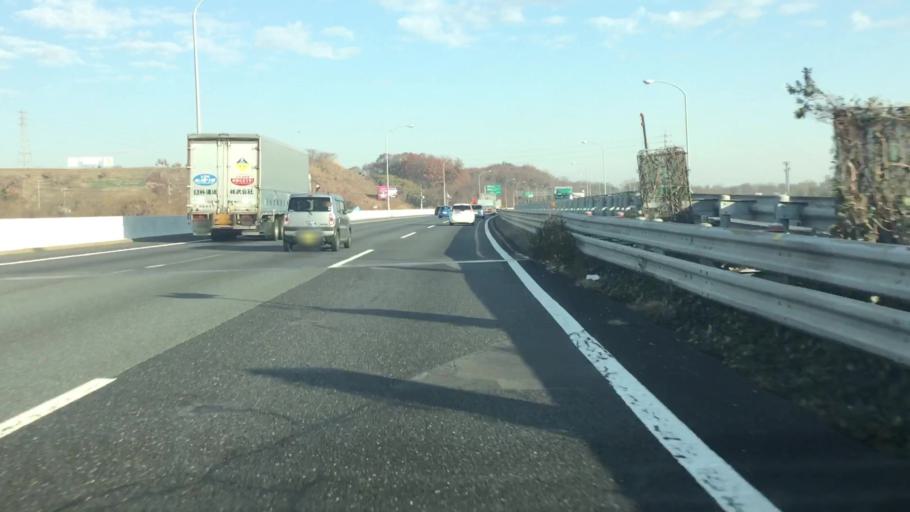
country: JP
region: Saitama
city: Sakado
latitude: 35.9798
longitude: 139.3801
